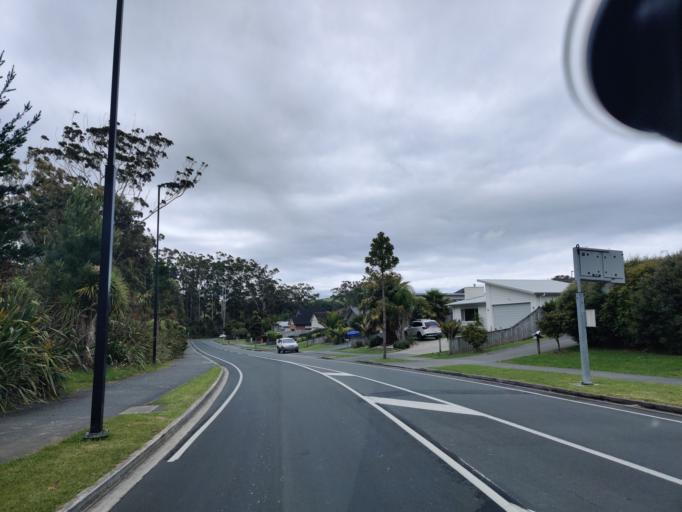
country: NZ
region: Auckland
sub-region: Auckland
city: Rothesay Bay
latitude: -36.6005
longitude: 174.6646
